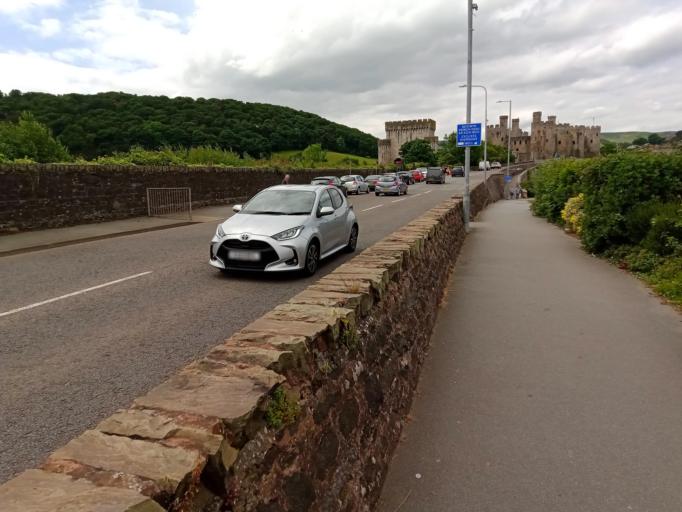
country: GB
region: Wales
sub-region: Conwy
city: Conwy
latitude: 53.2818
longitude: -3.8207
